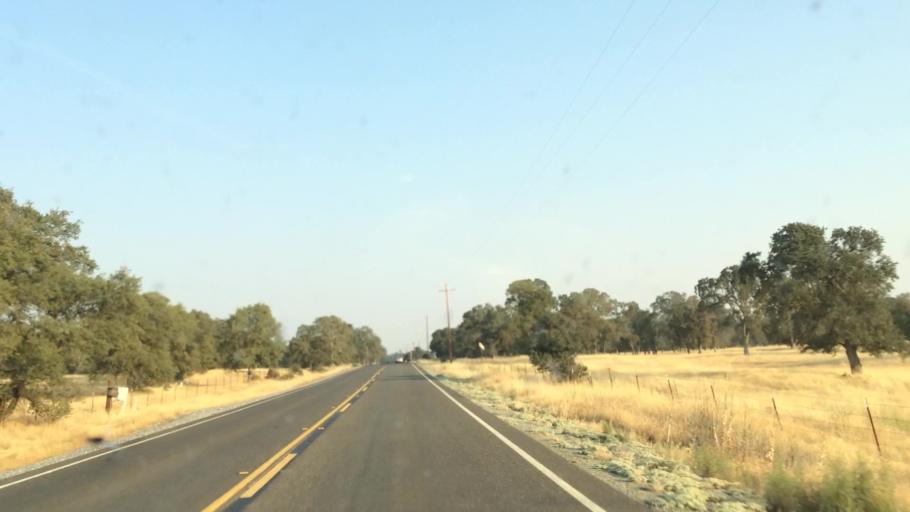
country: US
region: California
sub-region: Amador County
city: Ione
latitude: 38.3913
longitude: -120.9962
